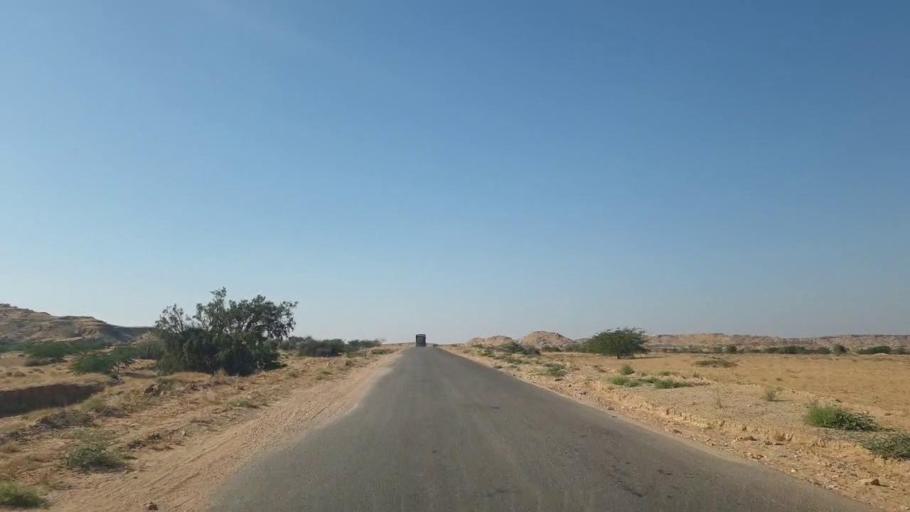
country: PK
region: Sindh
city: Gharo
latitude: 25.2190
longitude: 67.6229
